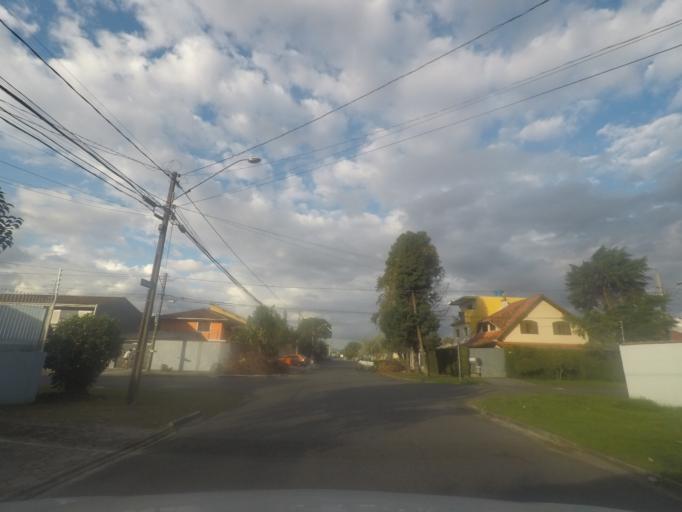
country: BR
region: Parana
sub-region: Pinhais
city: Pinhais
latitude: -25.4641
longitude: -49.2025
